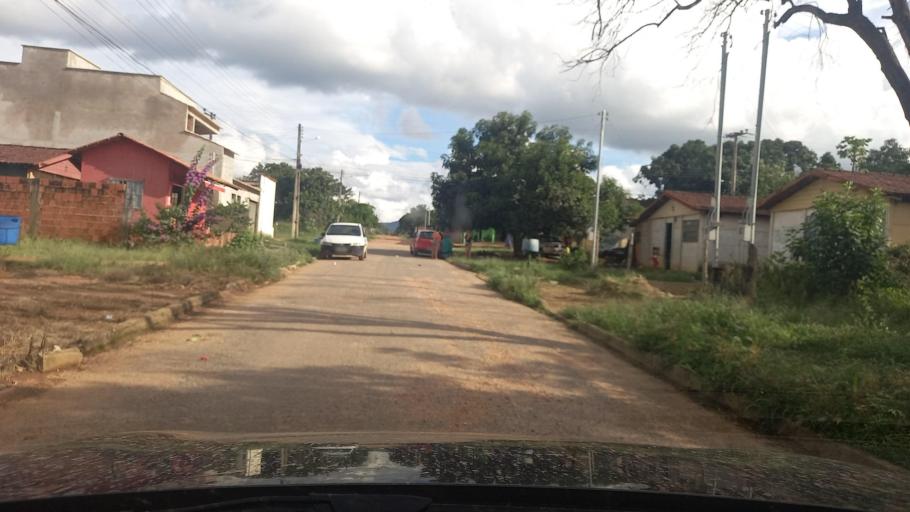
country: BR
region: Goias
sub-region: Cavalcante
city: Cavalcante
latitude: -13.7968
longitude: -47.4451
